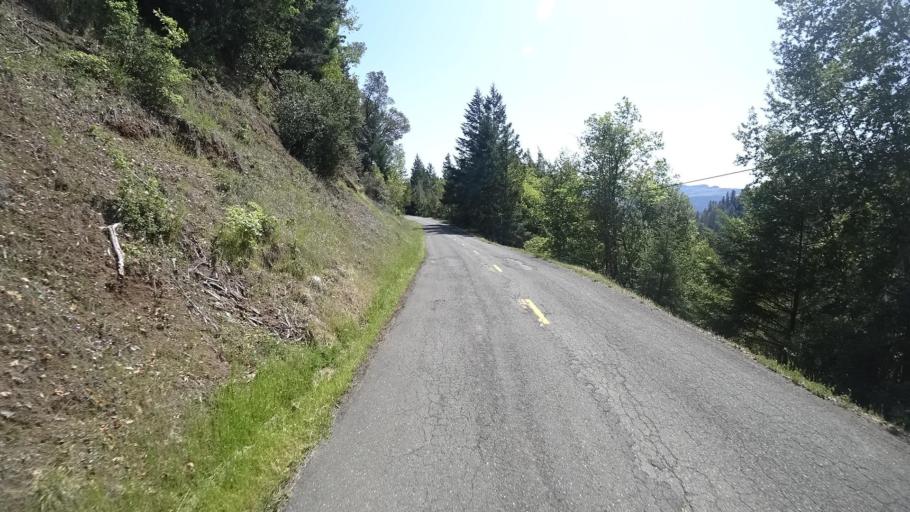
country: US
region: California
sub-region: Humboldt County
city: Redway
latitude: 40.2657
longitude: -123.6277
